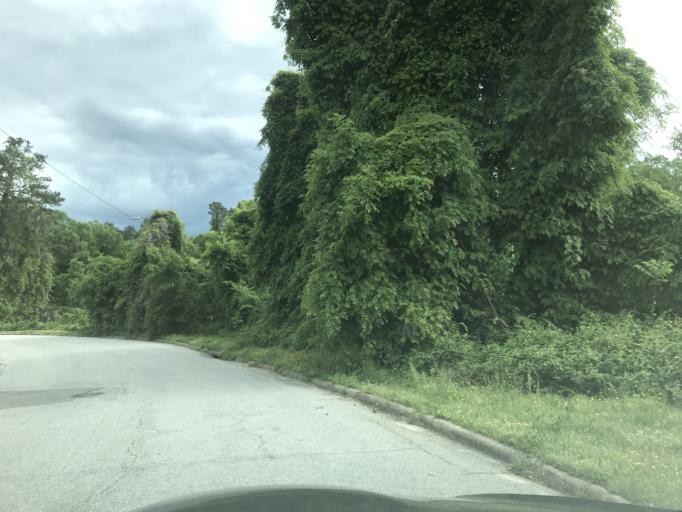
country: US
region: North Carolina
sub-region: Wake County
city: Raleigh
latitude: 35.7851
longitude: -78.5989
